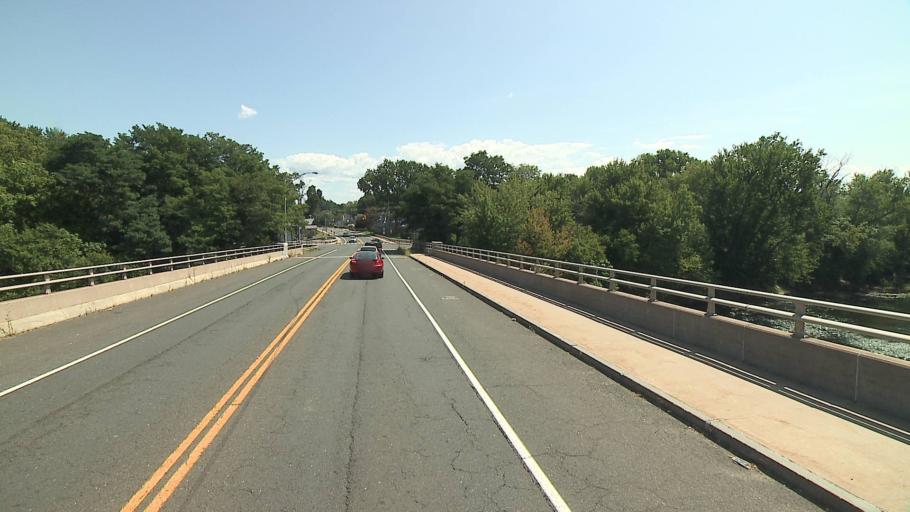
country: US
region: Connecticut
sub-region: Hartford County
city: Windsor Locks
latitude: 41.9291
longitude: -72.6228
